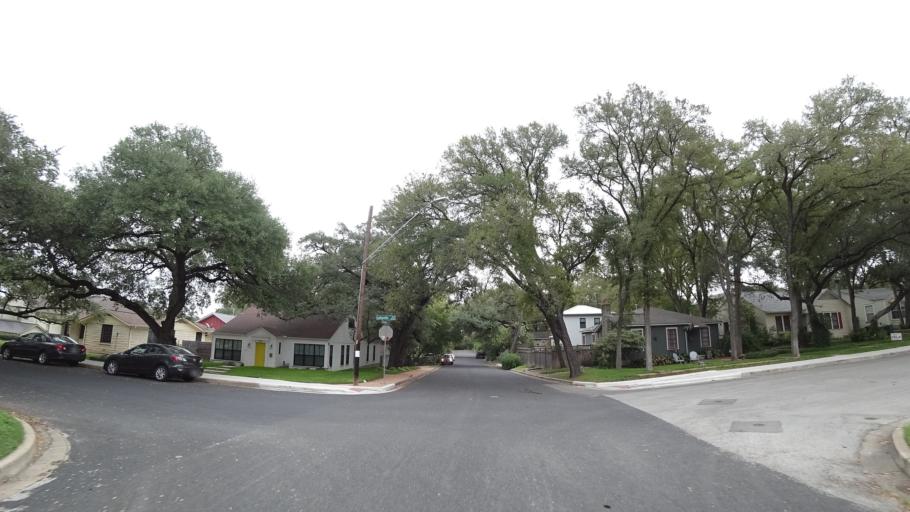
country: US
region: Texas
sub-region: Travis County
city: Austin
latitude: 30.2894
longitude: -97.7190
